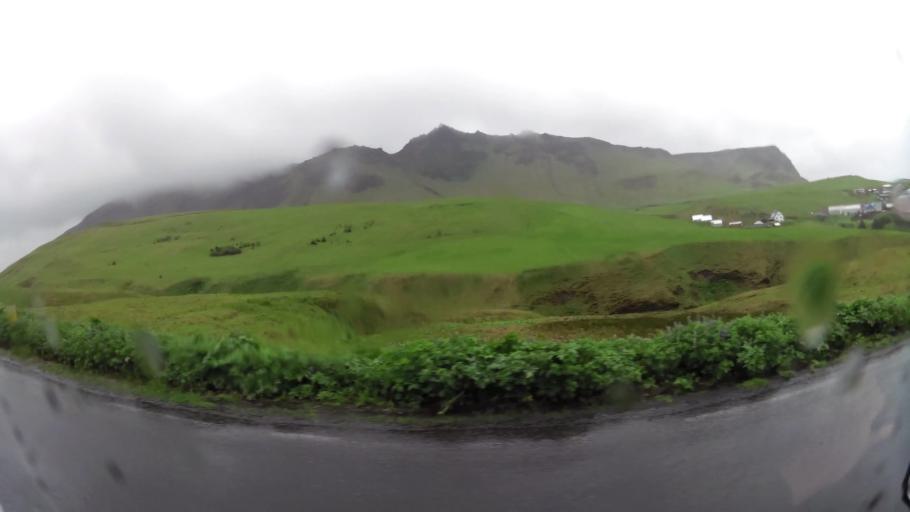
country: IS
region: South
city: Vestmannaeyjar
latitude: 63.4234
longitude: -19.0165
